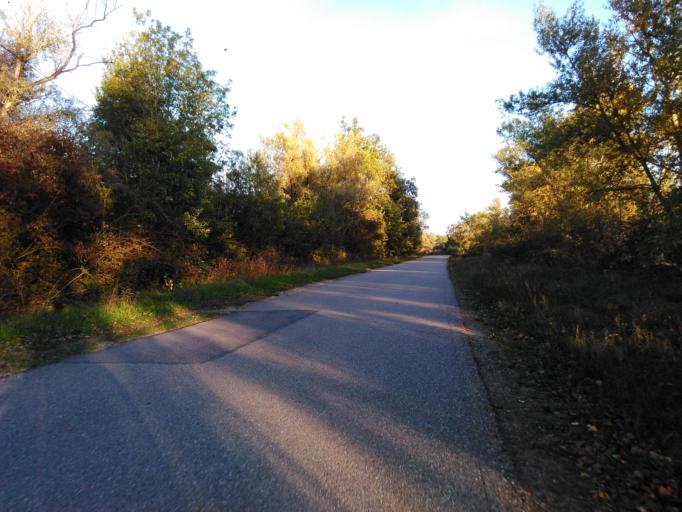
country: FR
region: Lorraine
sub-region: Departement de la Moselle
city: Argancy
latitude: 49.1947
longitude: 6.1896
